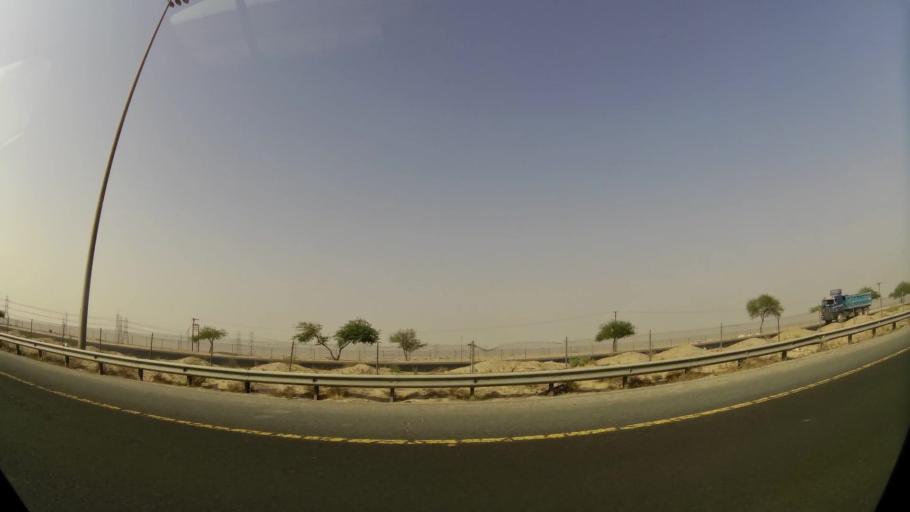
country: KW
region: Al Asimah
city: Ar Rabiyah
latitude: 29.1946
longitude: 47.8819
